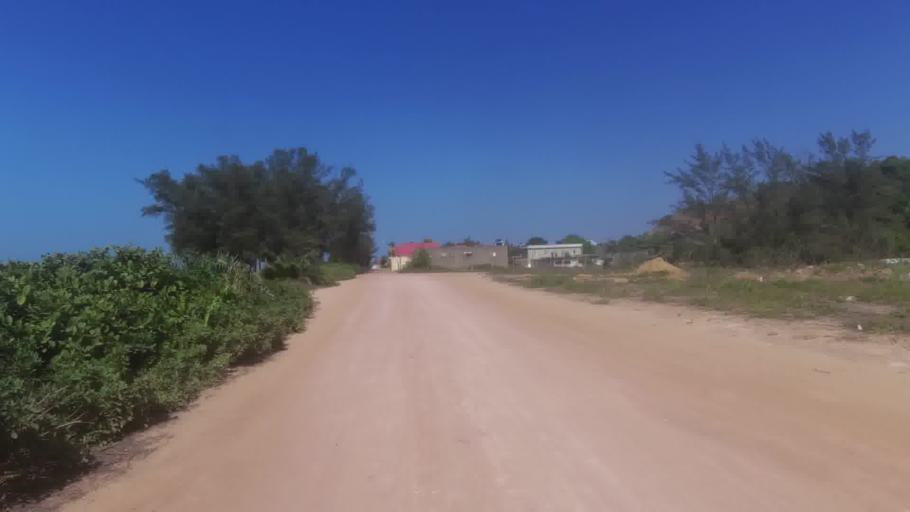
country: BR
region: Espirito Santo
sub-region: Marataizes
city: Marataizes
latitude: -21.1036
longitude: -40.8504
